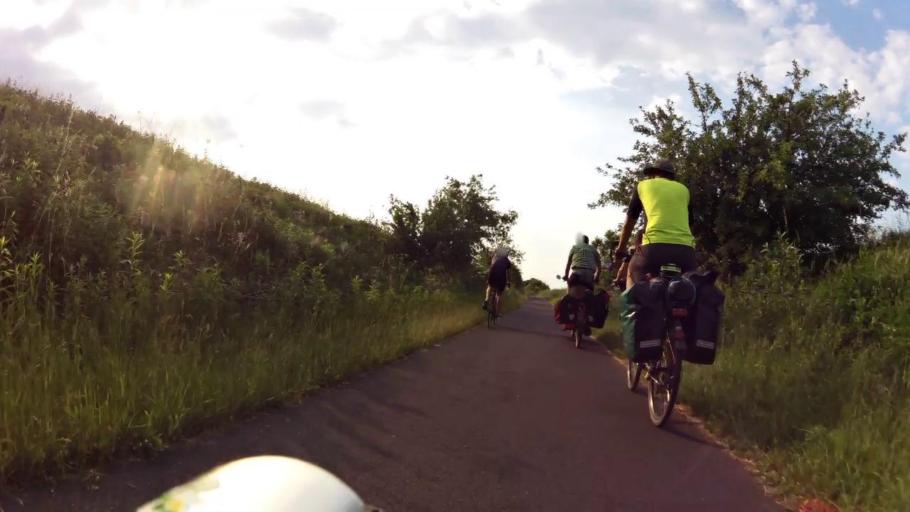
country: PL
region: Kujawsko-Pomorskie
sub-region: Powiat torunski
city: Lubianka
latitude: 53.1495
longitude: 18.4569
